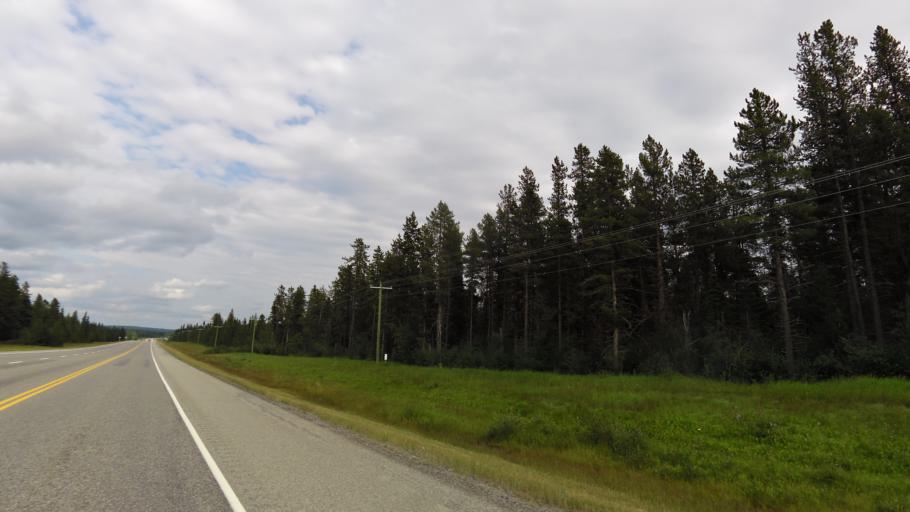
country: CA
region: Alberta
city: Rocky Mountain House
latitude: 52.4926
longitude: -115.6001
